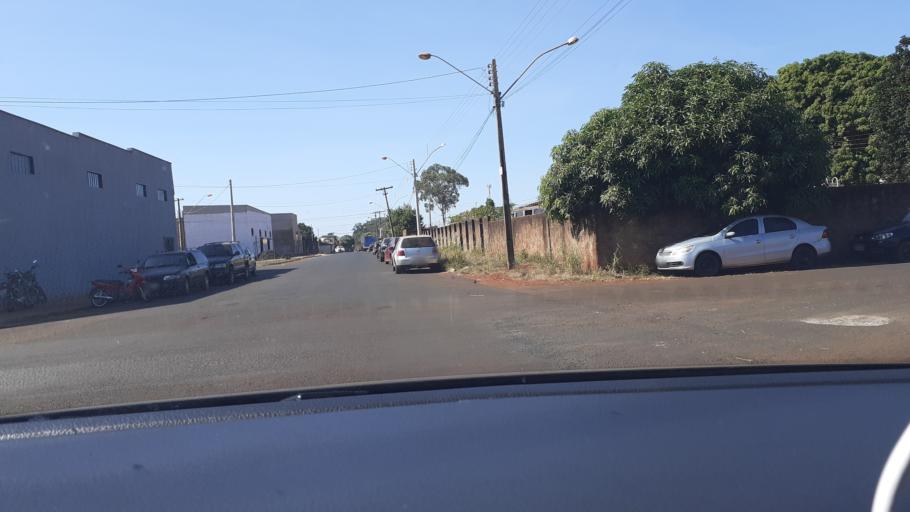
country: BR
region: Goias
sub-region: Itumbiara
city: Itumbiara
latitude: -18.4117
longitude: -49.2401
